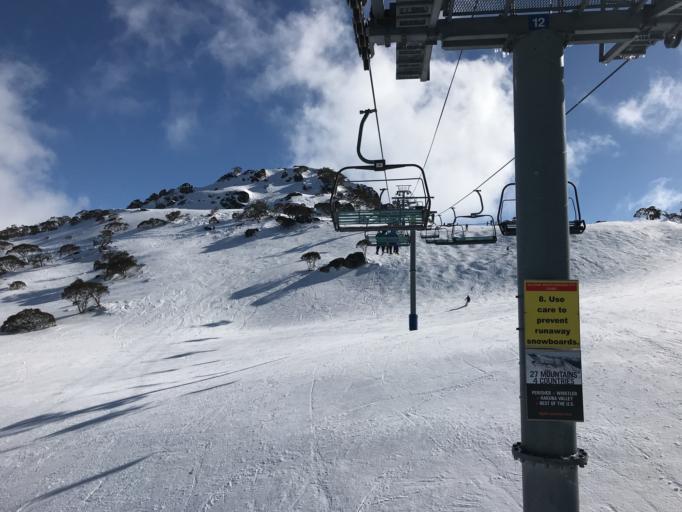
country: AU
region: New South Wales
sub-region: Snowy River
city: Jindabyne
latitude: -36.3932
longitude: 148.4021
